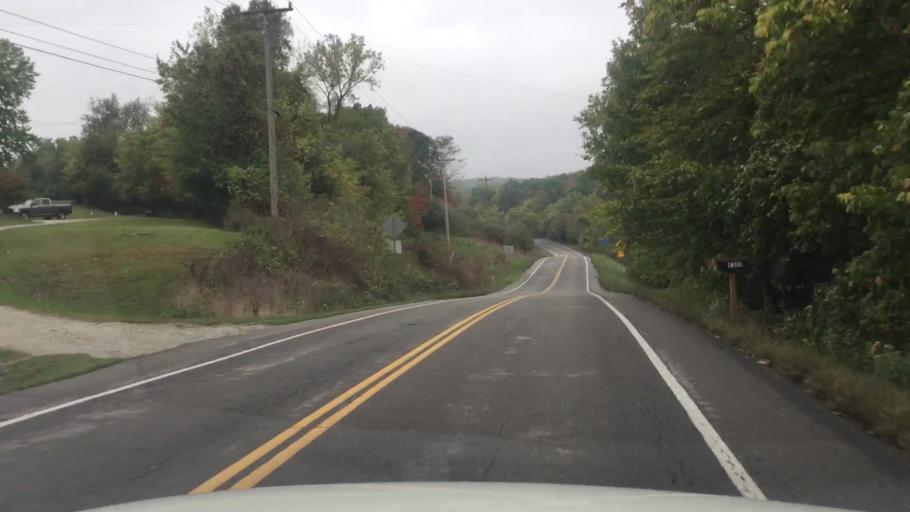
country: US
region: Missouri
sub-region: Boone County
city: Columbia
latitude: 38.8755
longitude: -92.4151
